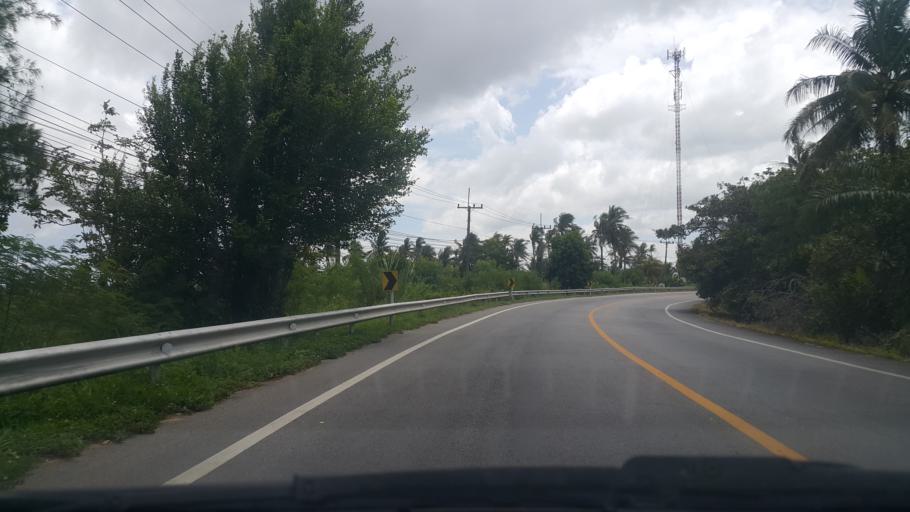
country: TH
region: Rayong
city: Ban Chang
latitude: 12.7826
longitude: 101.0247
